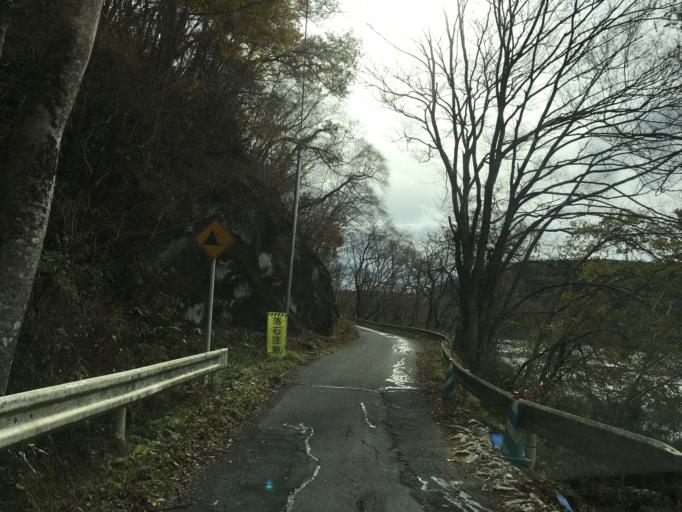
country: JP
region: Iwate
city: Ichinoseki
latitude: 38.7854
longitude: 141.2645
